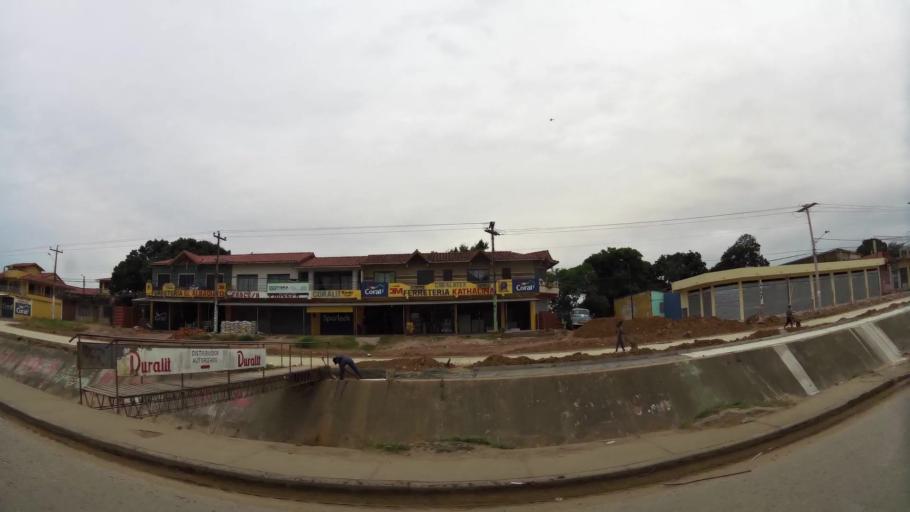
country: BO
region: Santa Cruz
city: Santa Cruz de la Sierra
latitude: -17.8548
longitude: -63.1791
